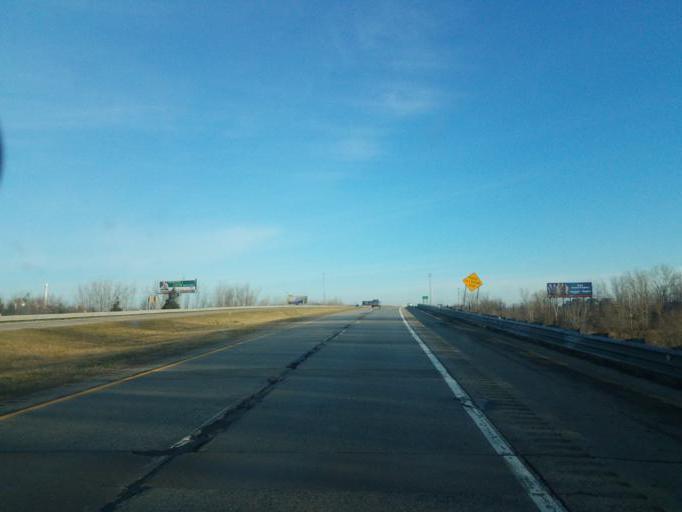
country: US
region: Michigan
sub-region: Ingham County
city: East Lansing
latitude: 42.7689
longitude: -84.5125
